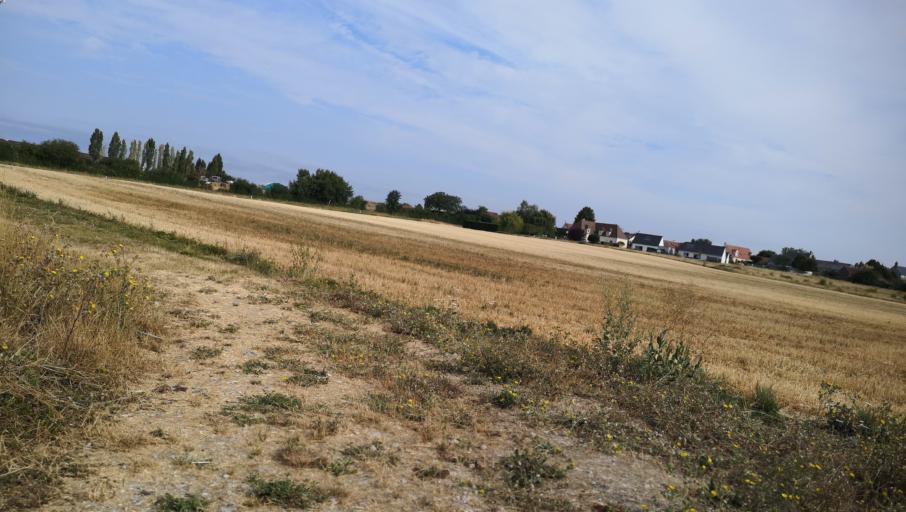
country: FR
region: Centre
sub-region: Departement du Loiret
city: Marigny-les-Usages
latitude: 47.9527
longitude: 2.0128
